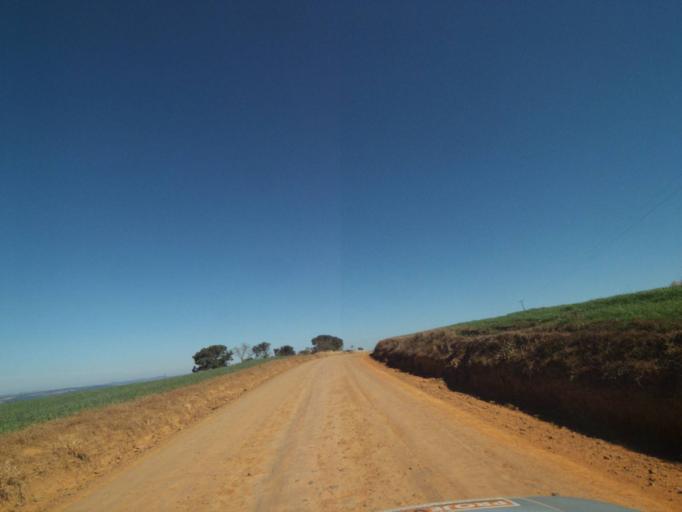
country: BR
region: Parana
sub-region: Tibagi
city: Tibagi
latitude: -24.6183
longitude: -50.6080
